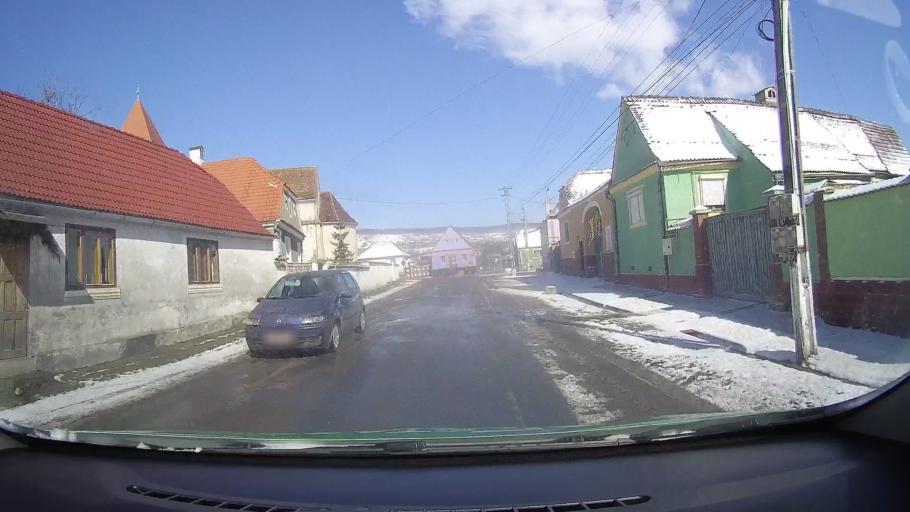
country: RO
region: Sibiu
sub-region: Comuna Avrig
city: Avrig
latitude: 45.7586
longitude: 24.3896
